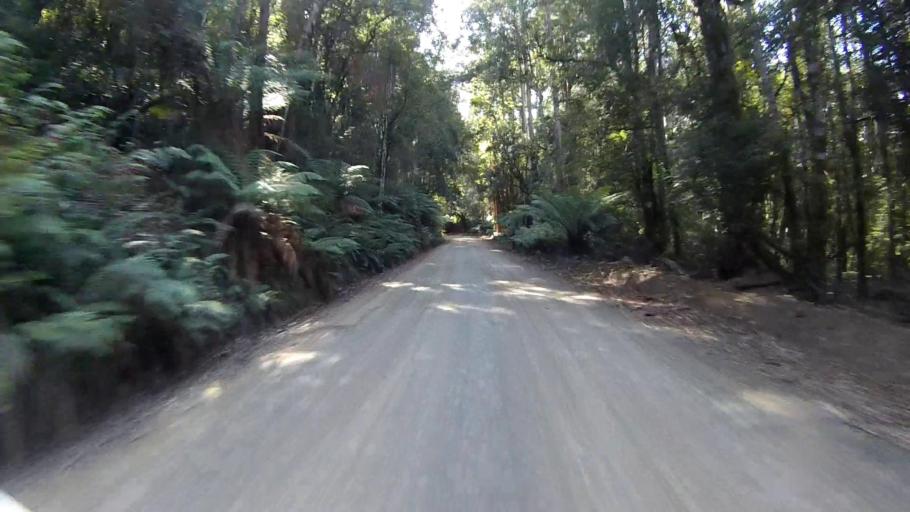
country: AU
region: Tasmania
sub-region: Derwent Valley
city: New Norfolk
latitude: -42.6786
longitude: 146.6977
